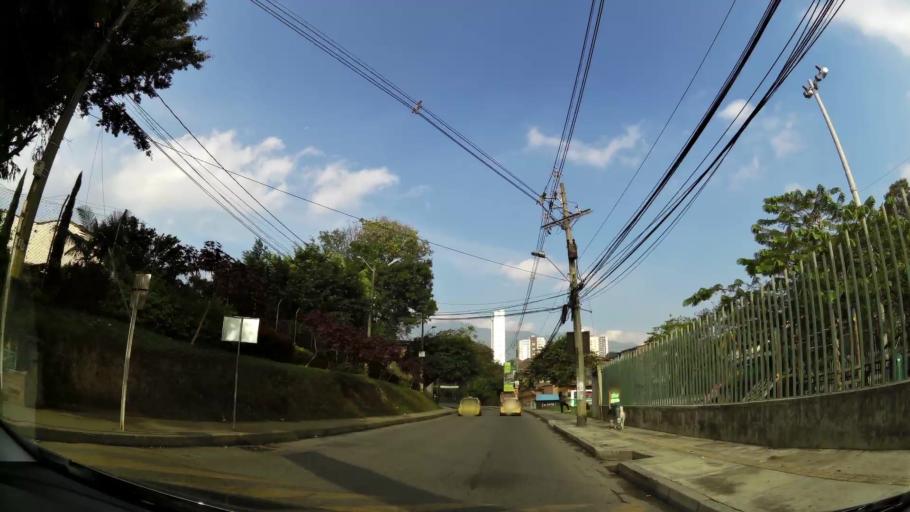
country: CO
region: Antioquia
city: Sabaneta
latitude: 6.1610
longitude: -75.6249
